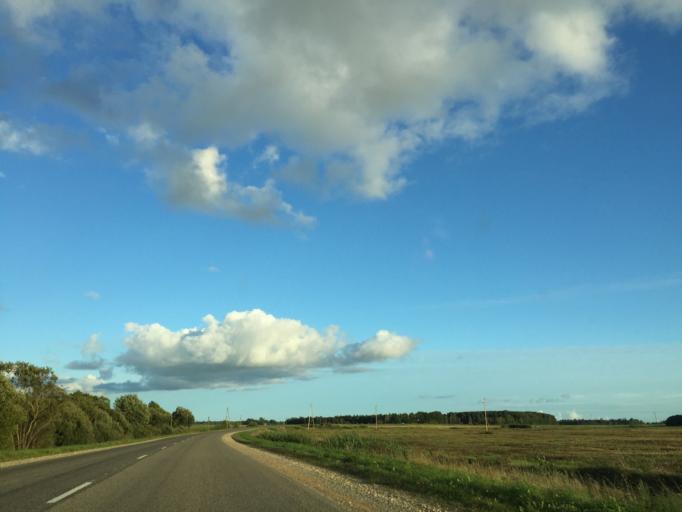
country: LV
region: Saldus Rajons
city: Saldus
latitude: 56.7511
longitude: 22.3704
